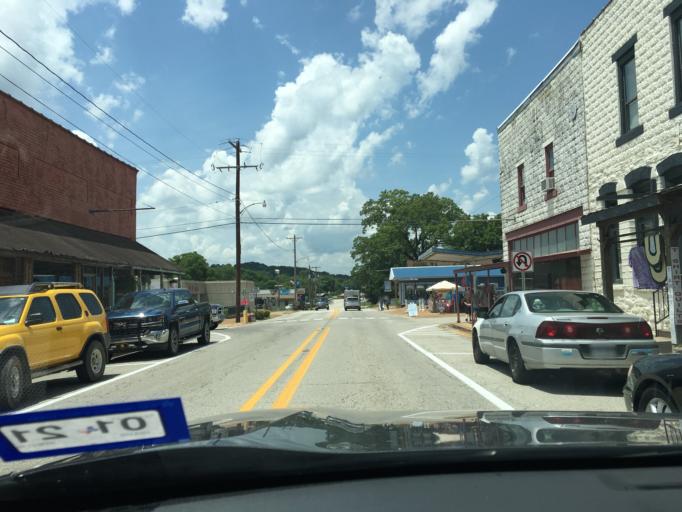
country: US
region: Arkansas
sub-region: Sharp County
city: Cherokee Village
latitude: 36.3156
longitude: -91.4822
